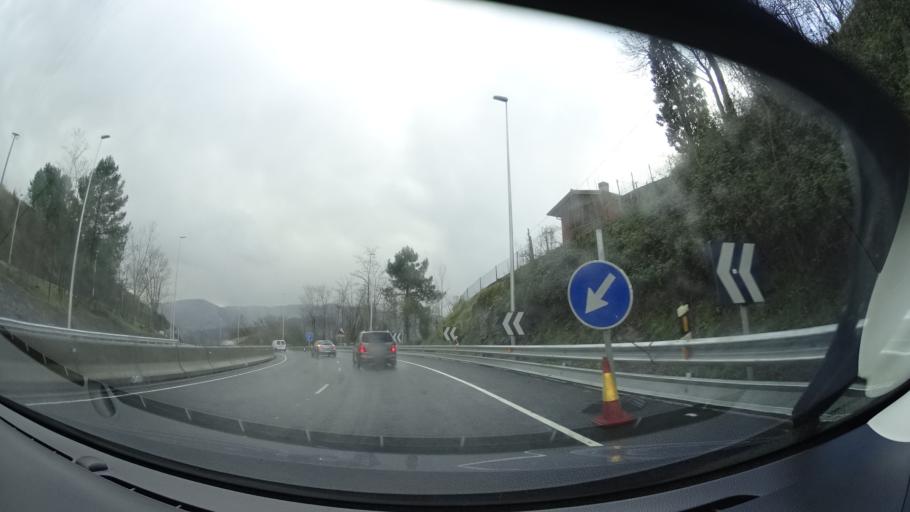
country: ES
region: Basque Country
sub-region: Bizkaia
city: Santutxu
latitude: 43.2697
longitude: -2.9064
